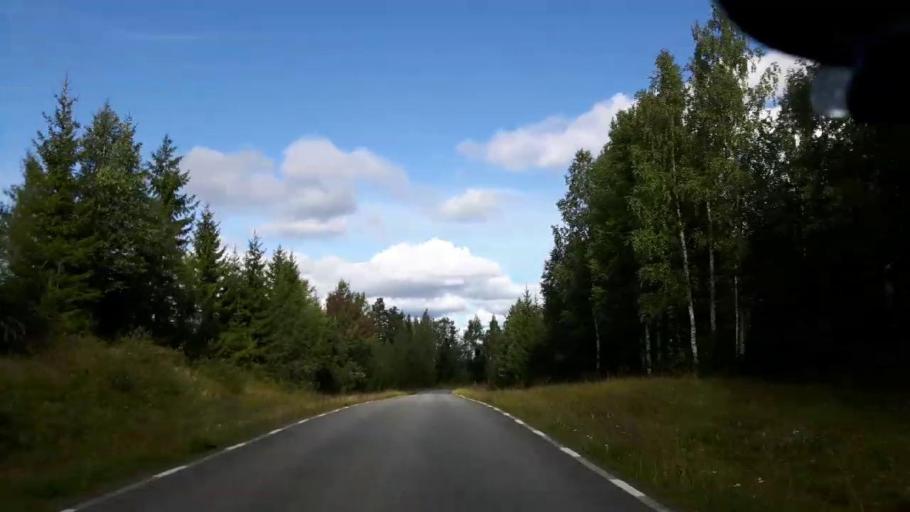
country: SE
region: Jaemtland
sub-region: OEstersunds Kommun
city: Brunflo
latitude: 63.2178
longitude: 15.2442
